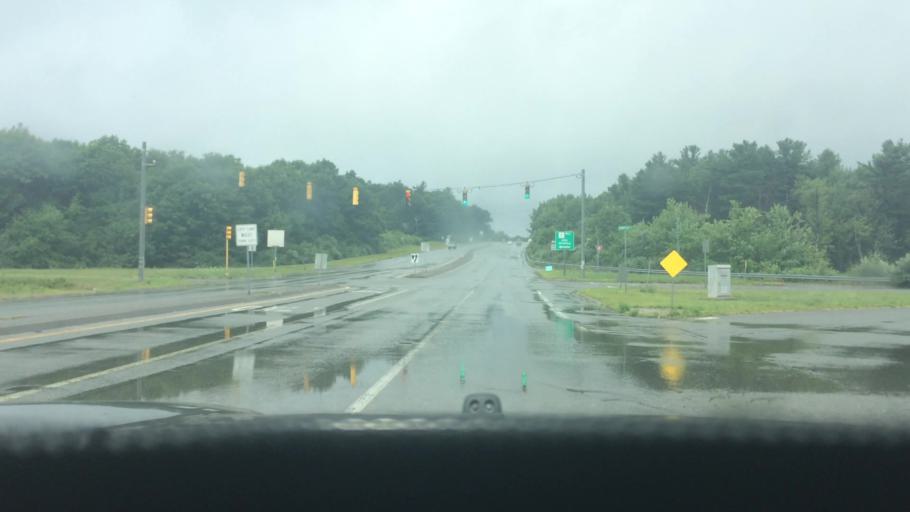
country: US
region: Massachusetts
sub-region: Worcester County
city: Westminster
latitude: 42.5613
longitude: -71.9353
